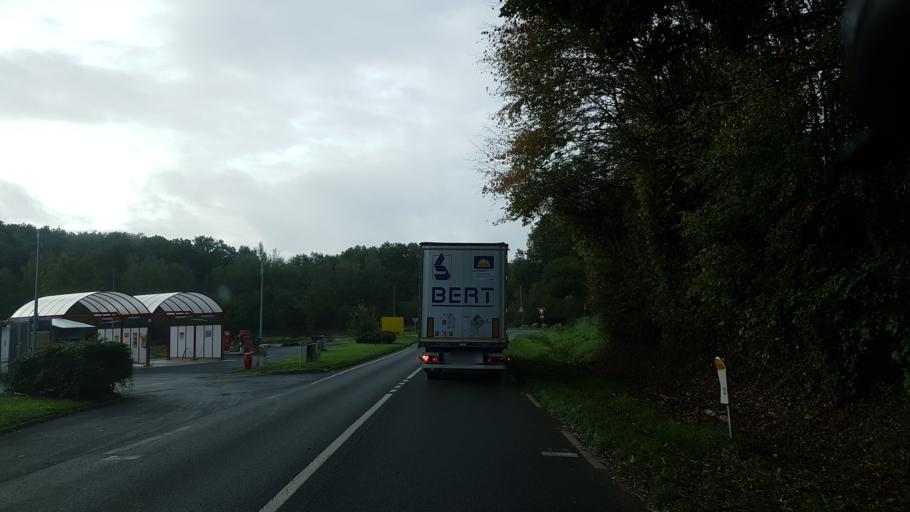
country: FR
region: Ile-de-France
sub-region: Departement de l'Essonne
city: Dourdan
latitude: 48.5193
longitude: 2.0186
